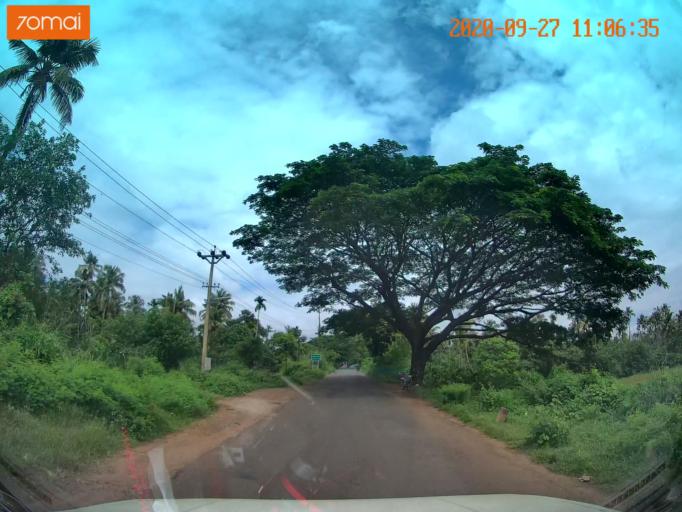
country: IN
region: Kerala
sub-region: Thrissur District
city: Irinjalakuda
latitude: 10.4262
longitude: 76.2410
